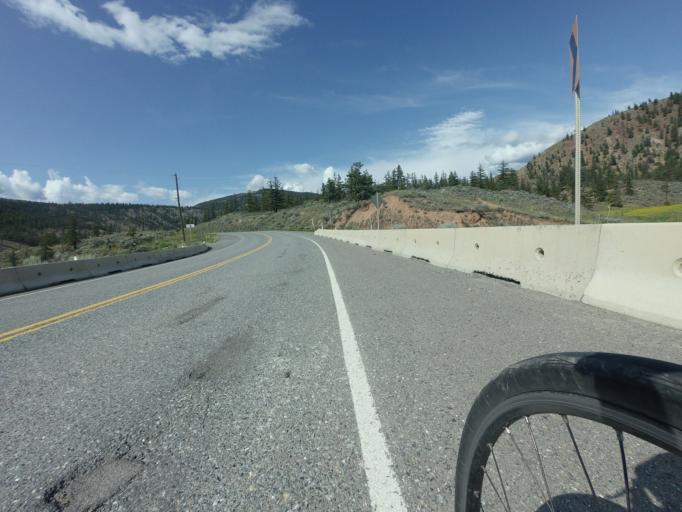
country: CA
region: British Columbia
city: Lillooet
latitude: 50.8721
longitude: -121.8313
